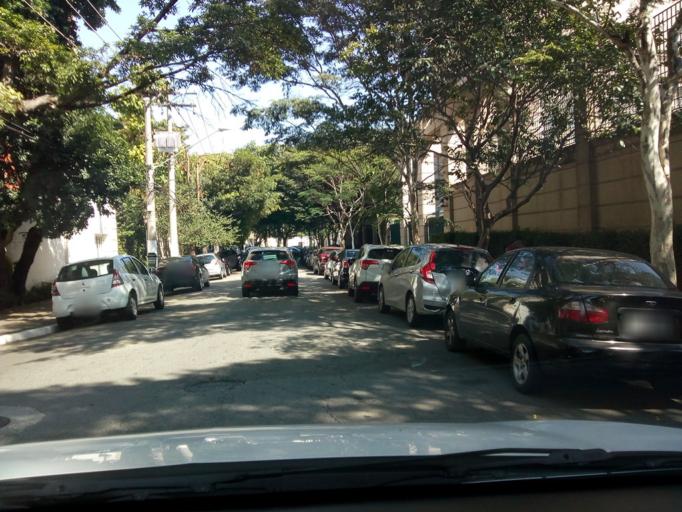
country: BR
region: Sao Paulo
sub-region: Sao Paulo
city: Sao Paulo
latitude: -23.5801
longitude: -46.6536
